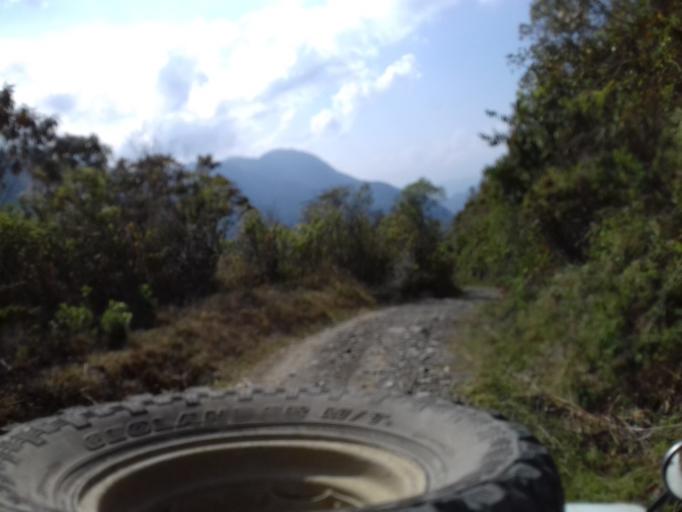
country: CO
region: Tolima
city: Cajamarca
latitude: 4.5329
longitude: -75.4182
